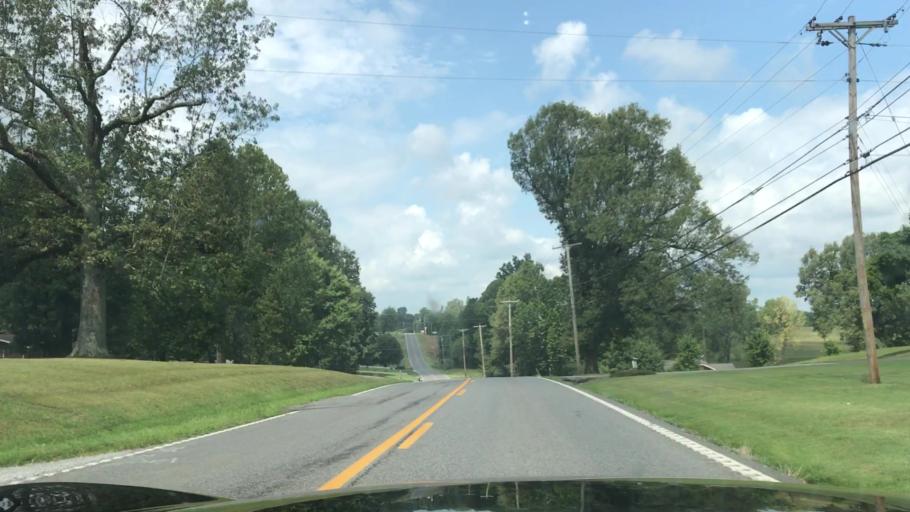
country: US
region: Kentucky
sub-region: Muhlenberg County
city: Greenville
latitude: 37.2052
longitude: -87.1472
